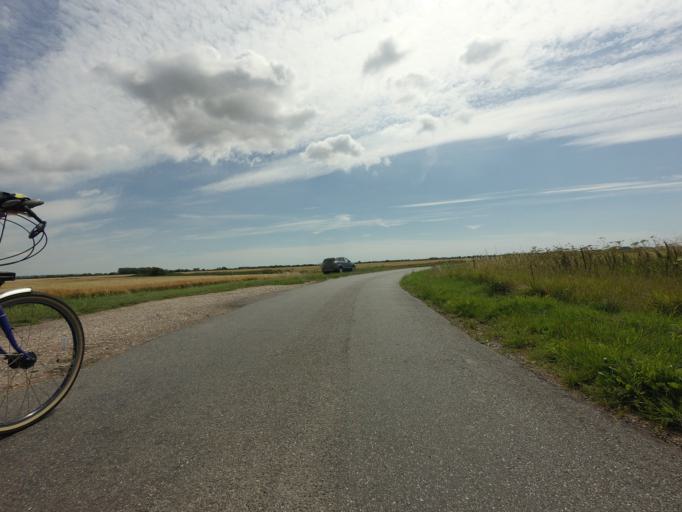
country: GB
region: England
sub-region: Kent
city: Stone
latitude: 51.0256
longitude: 0.7965
